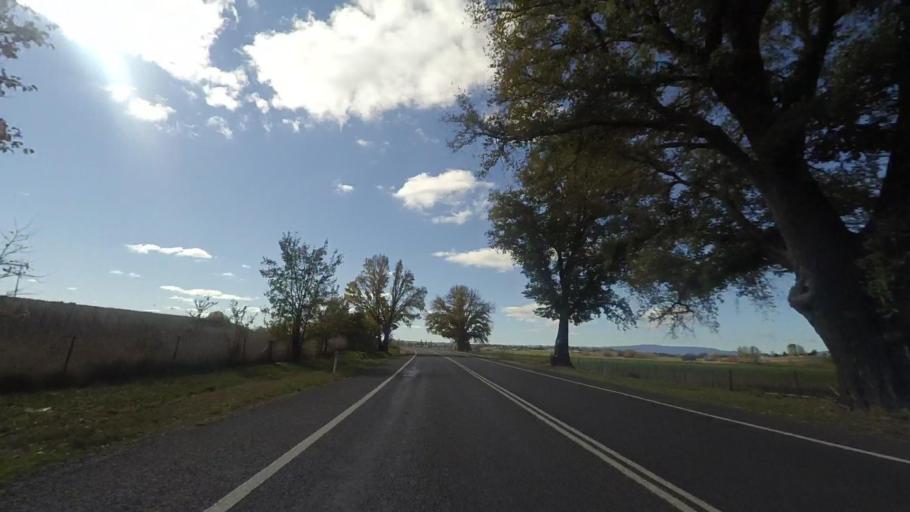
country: AU
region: New South Wales
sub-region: Bathurst Regional
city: Bathurst
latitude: -33.4522
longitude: 149.5781
